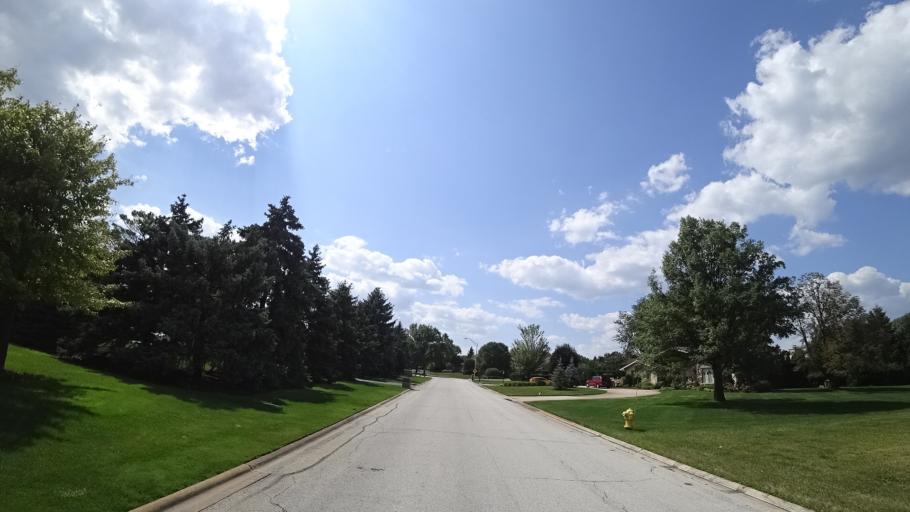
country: US
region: Illinois
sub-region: Cook County
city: Orland Park
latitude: 41.6265
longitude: -87.8234
